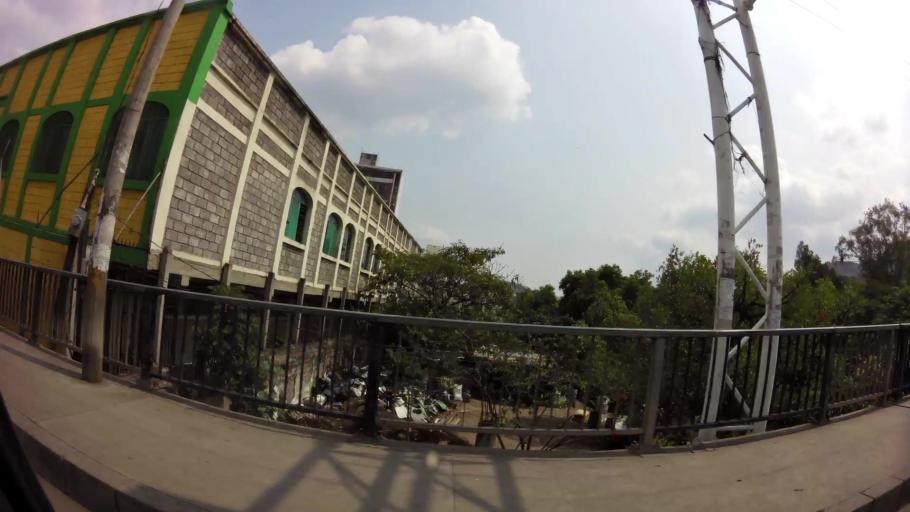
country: HN
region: Francisco Morazan
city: Tegucigalpa
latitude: 14.1102
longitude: -87.2093
